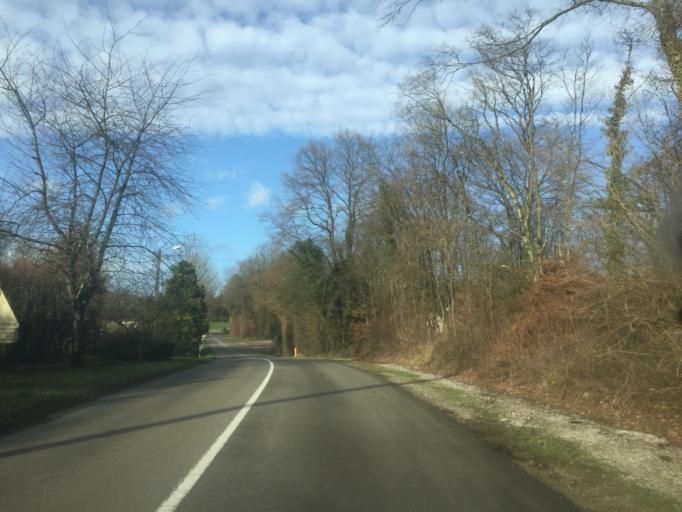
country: FR
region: Franche-Comte
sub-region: Departement du Doubs
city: Saint-Vit
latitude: 47.1863
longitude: 5.8114
